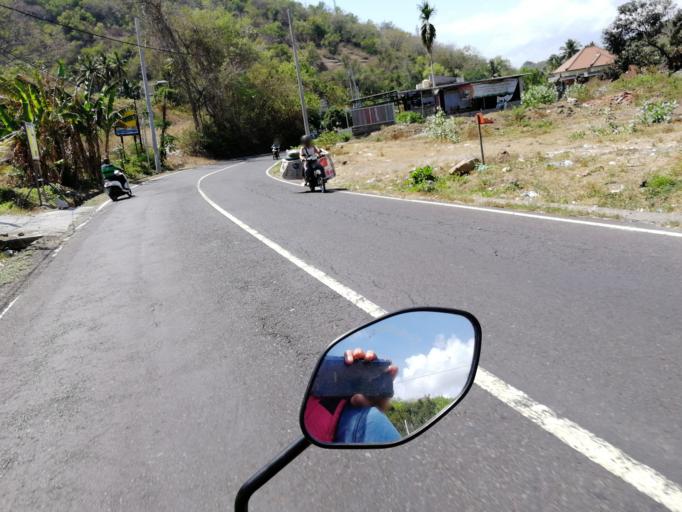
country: ID
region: Bali
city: Padangbai
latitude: -8.5244
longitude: 115.5034
